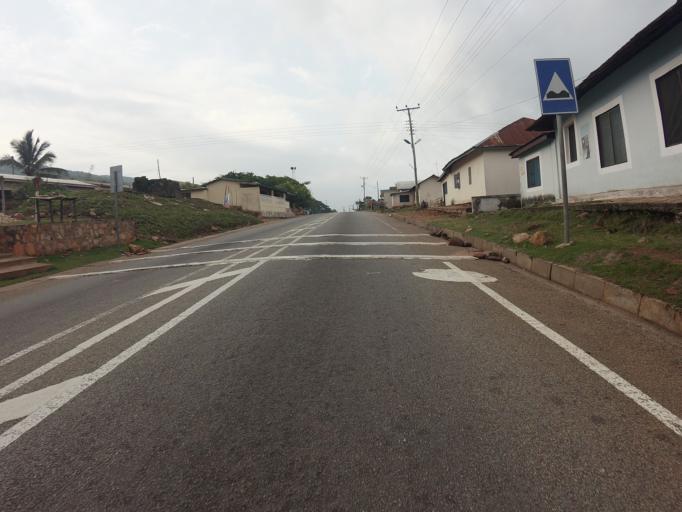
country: GH
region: Volta
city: Ho
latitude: 6.6584
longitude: 0.4714
